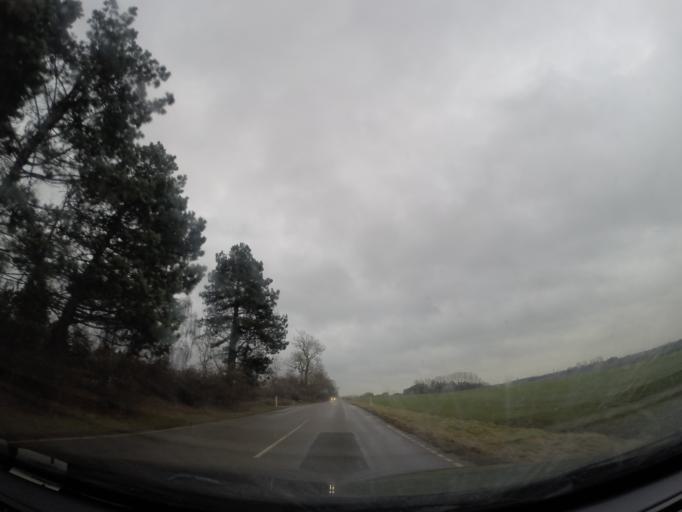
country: DK
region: Capital Region
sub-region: Hoje-Taastrup Kommune
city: Taastrup
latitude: 55.6828
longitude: 12.3051
